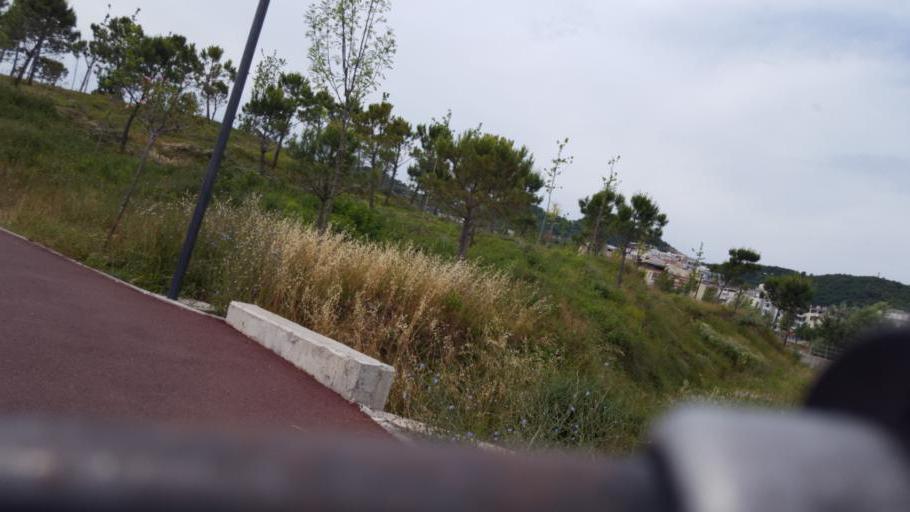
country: AL
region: Tirane
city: Tirana
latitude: 41.3064
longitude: 19.8200
